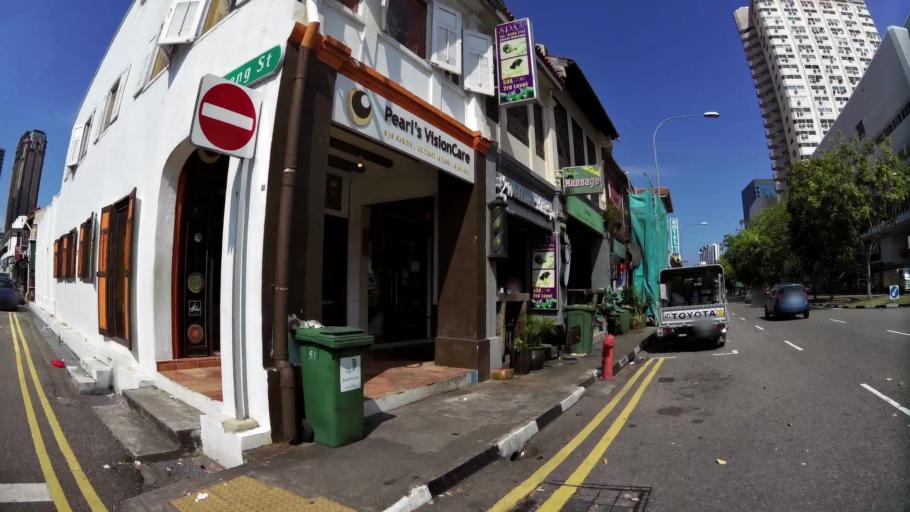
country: SG
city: Singapore
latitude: 1.3025
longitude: 103.8616
